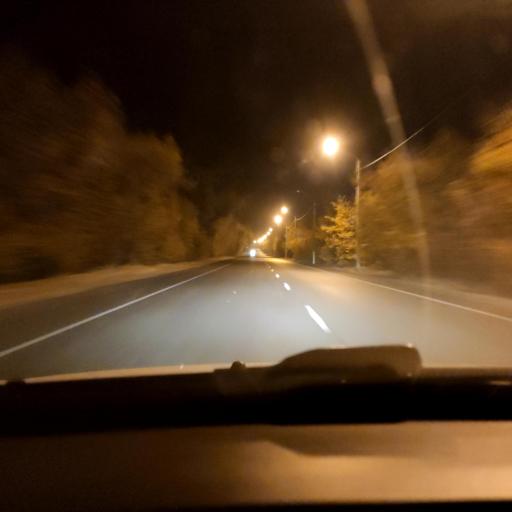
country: RU
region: Voronezj
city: Voronezh
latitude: 51.6069
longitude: 39.1791
